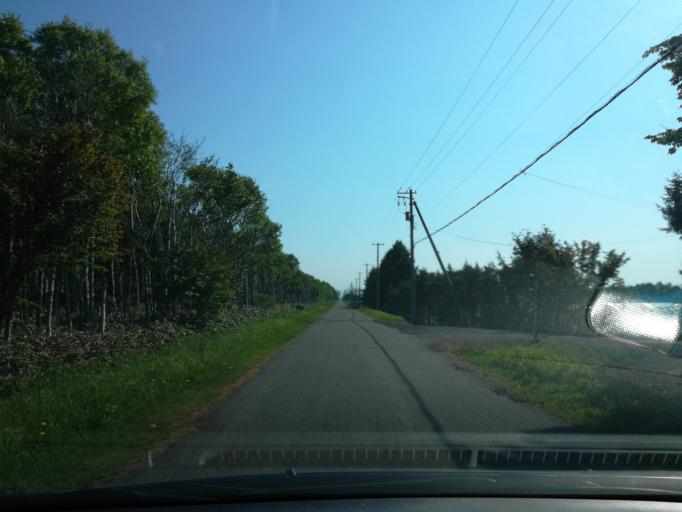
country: JP
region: Hokkaido
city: Ebetsu
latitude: 43.1173
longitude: 141.6495
